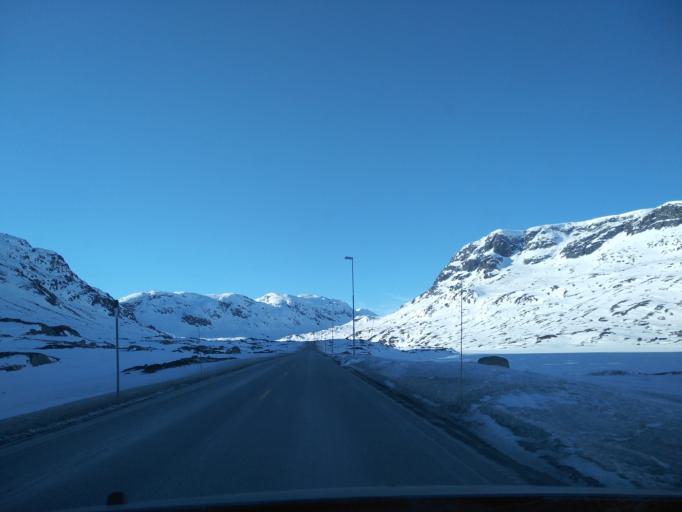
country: NO
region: Aust-Agder
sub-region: Bykle
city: Hovden
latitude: 59.8492
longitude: 7.1200
